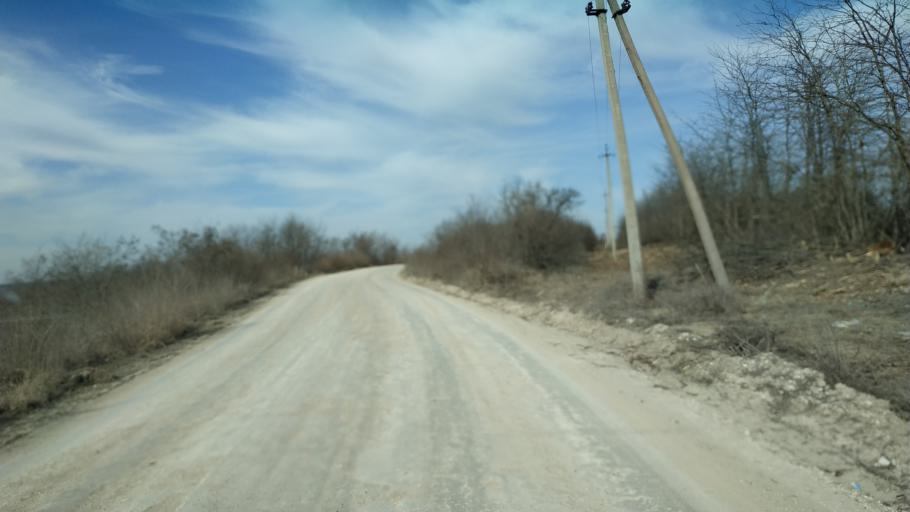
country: MD
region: Nisporeni
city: Nisporeni
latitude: 46.9659
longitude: 28.2015
